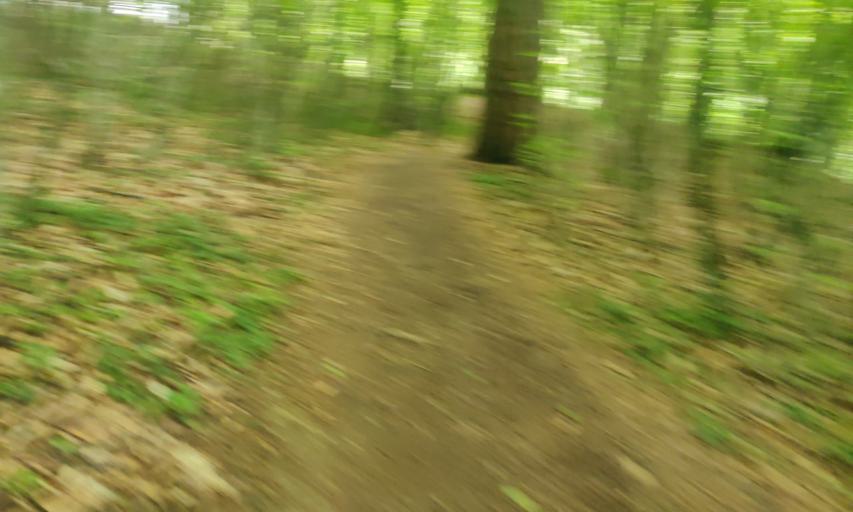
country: CH
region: Fribourg
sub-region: Sarine District
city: Marly
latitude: 46.7868
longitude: 7.1576
